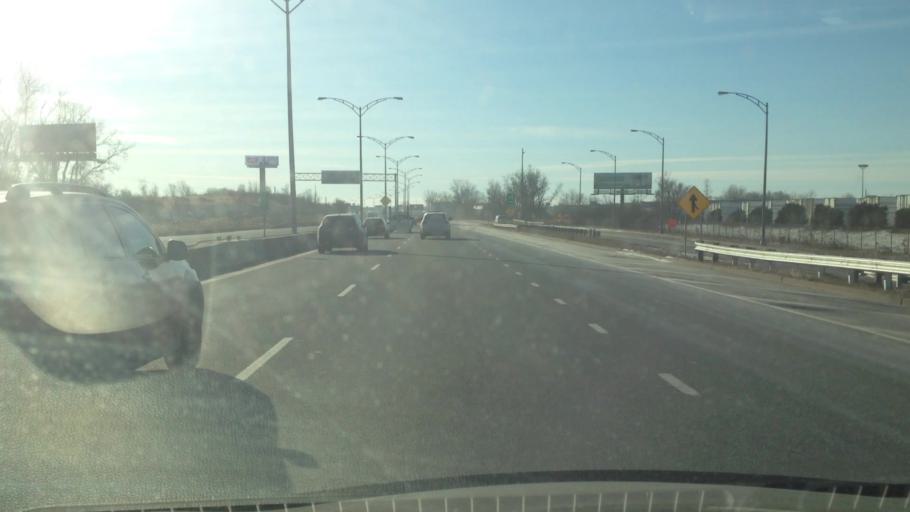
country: CA
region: Quebec
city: Cote-Saint-Luc
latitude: 45.4611
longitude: -73.6963
